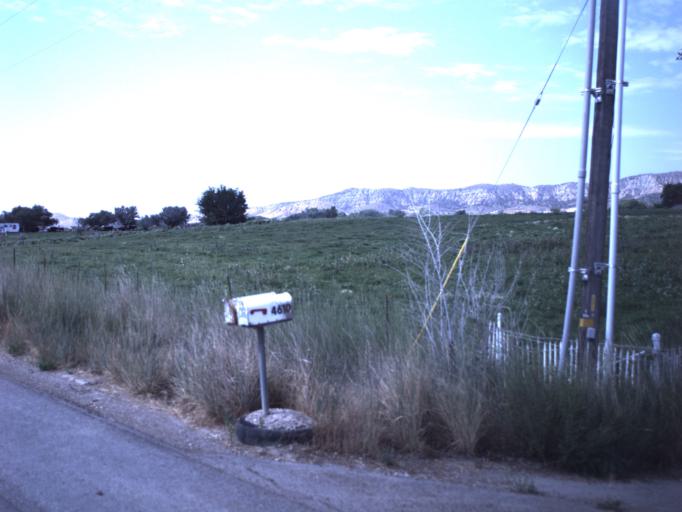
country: US
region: Utah
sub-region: Uintah County
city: Naples
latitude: 40.3885
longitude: -109.4988
